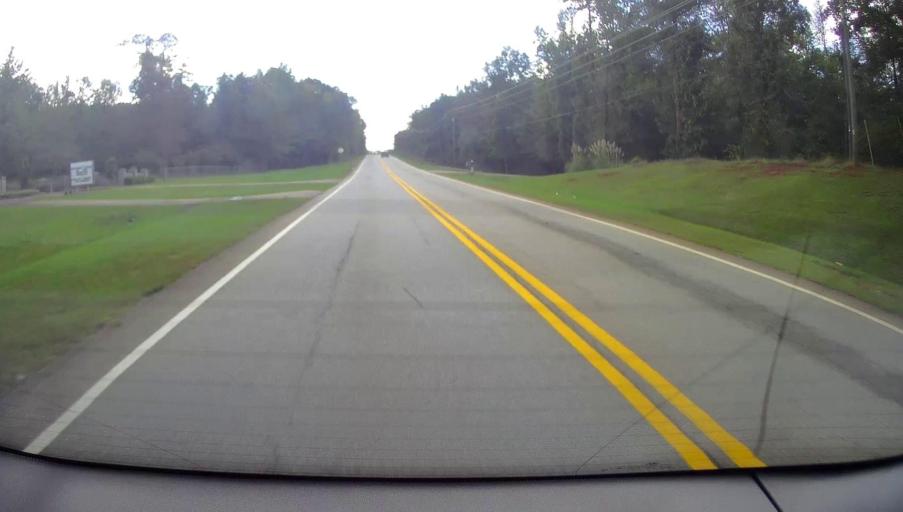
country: US
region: Georgia
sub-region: Jones County
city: Gray
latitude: 32.9747
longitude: -83.4227
